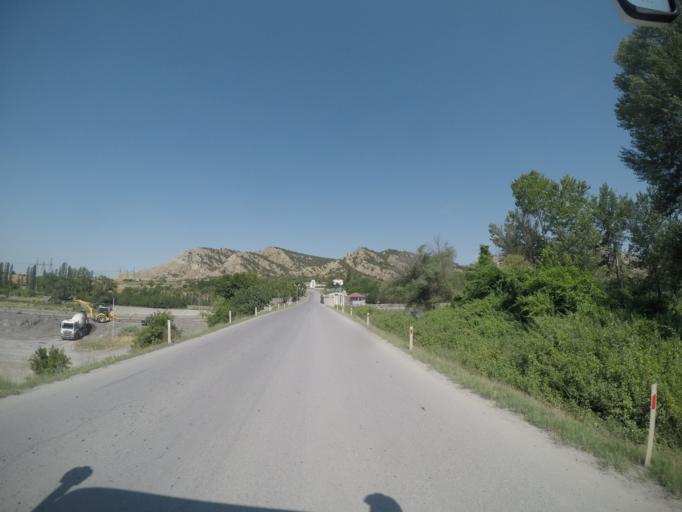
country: AZ
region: Agdas
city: Agdas
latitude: 40.7114
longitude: 47.5497
